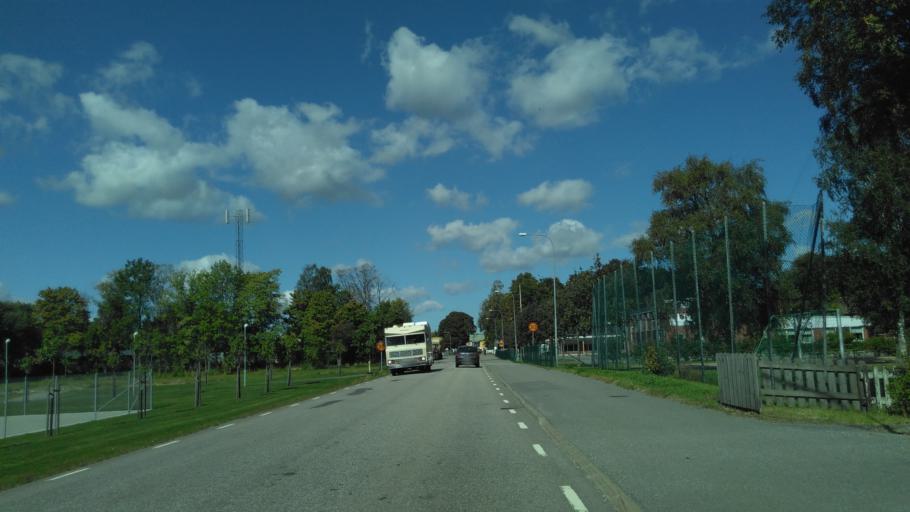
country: SE
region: Vaestra Goetaland
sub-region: Herrljunga Kommun
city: Herrljunga
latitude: 58.1678
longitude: 13.0011
